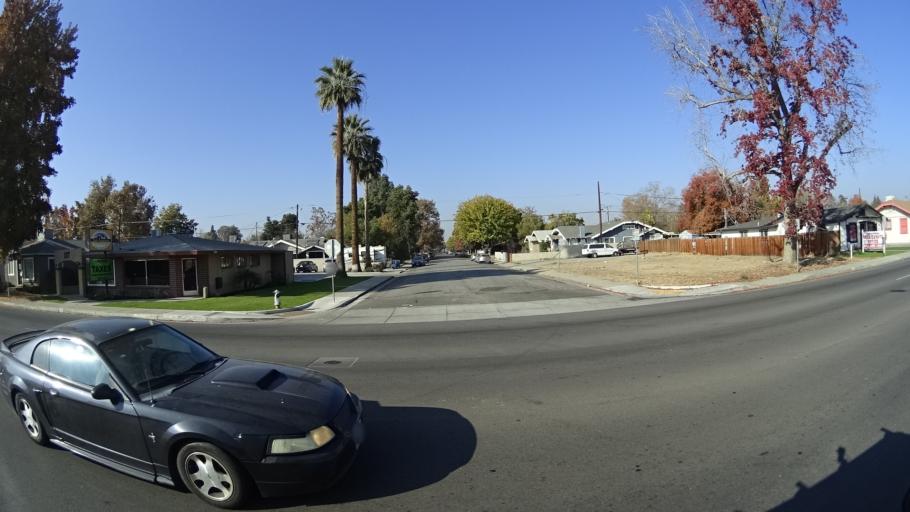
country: US
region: California
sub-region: Kern County
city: Bakersfield
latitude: 35.3559
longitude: -119.0213
